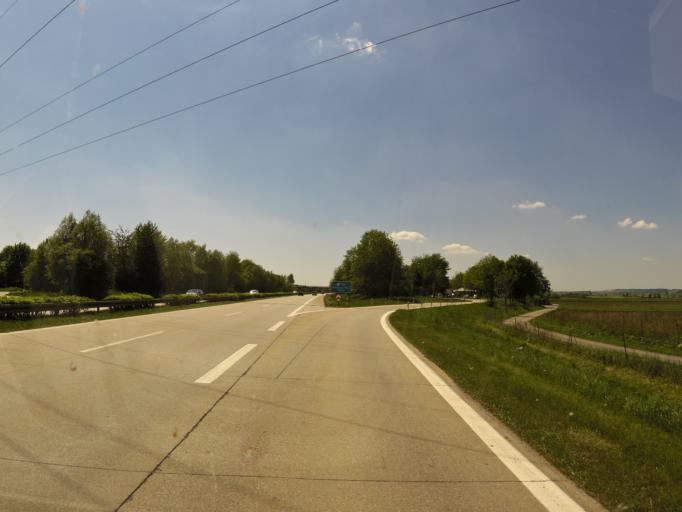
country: DE
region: Bavaria
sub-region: Lower Bavaria
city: Dingolfing
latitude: 48.6522
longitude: 12.4548
